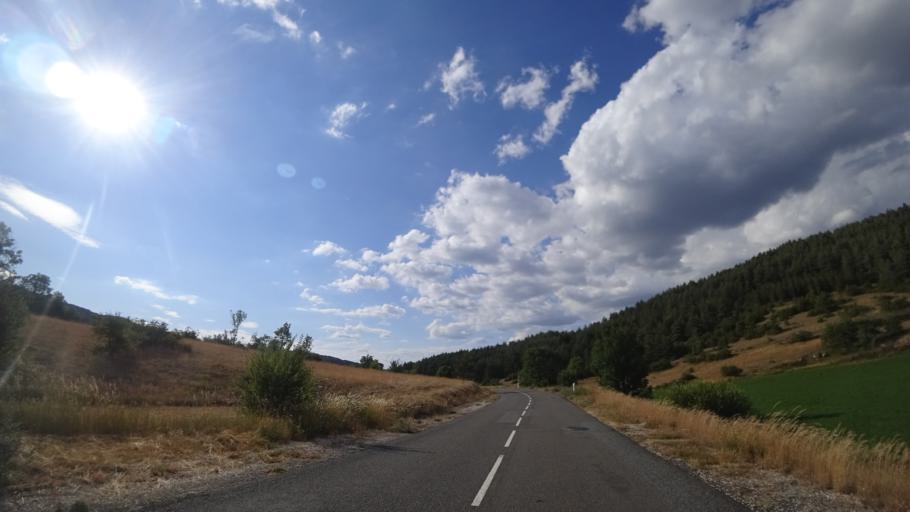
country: FR
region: Languedoc-Roussillon
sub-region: Departement de la Lozere
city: Chanac
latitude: 44.3896
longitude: 3.3021
